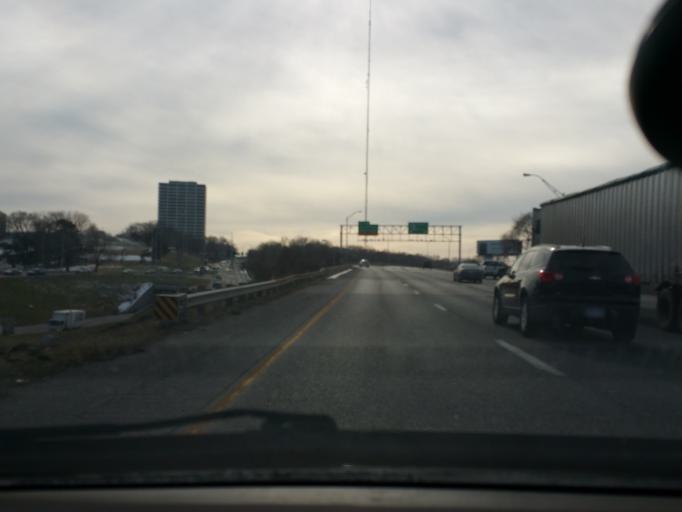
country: US
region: Missouri
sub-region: Jackson County
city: Kansas City
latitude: 39.0807
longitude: -94.5938
